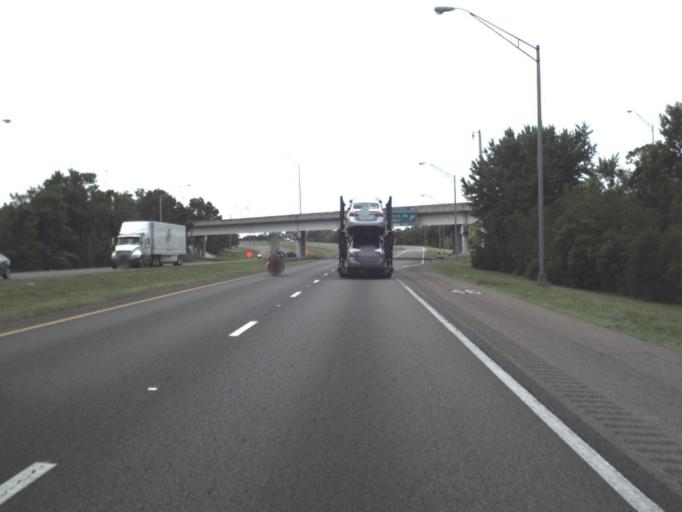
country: US
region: Florida
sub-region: Duval County
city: Jacksonville
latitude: 30.3590
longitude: -81.5544
